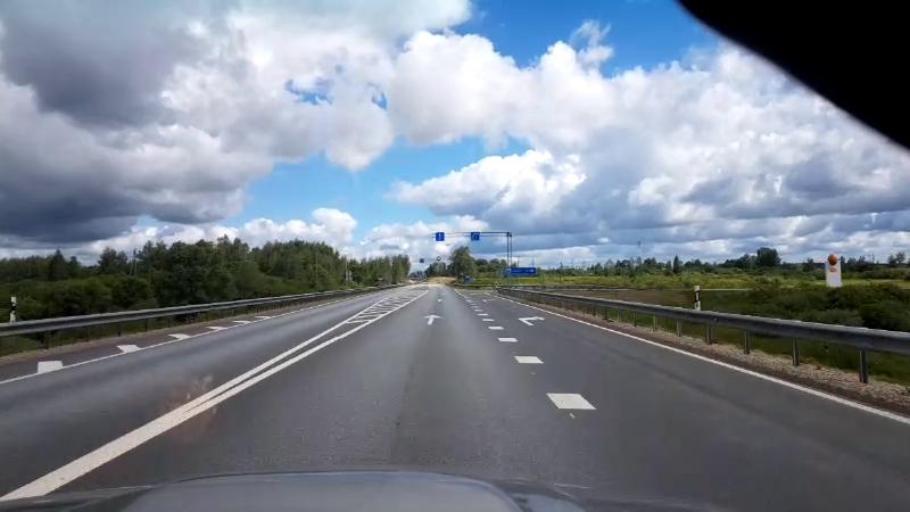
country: LV
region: Lecava
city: Iecava
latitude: 56.6253
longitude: 24.2206
